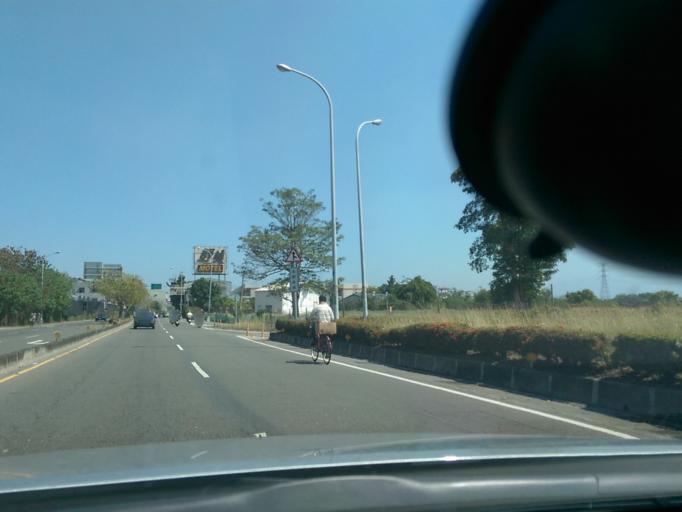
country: TW
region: Taiwan
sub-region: Chiayi
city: Jiayi Shi
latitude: 23.4316
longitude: 120.4504
